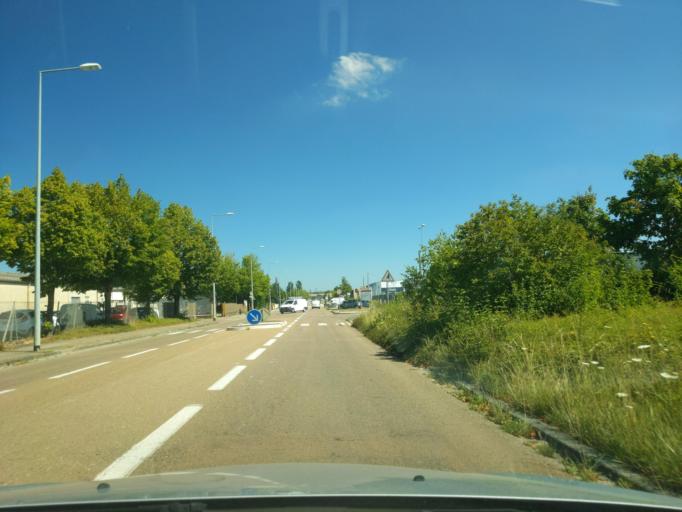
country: FR
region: Bourgogne
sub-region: Departement de la Cote-d'Or
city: Saint-Apollinaire
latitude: 47.3437
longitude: 5.0628
